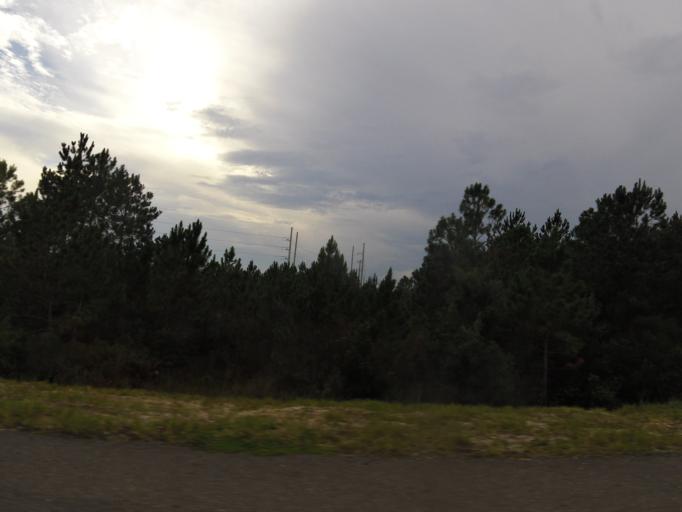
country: US
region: Florida
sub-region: Duval County
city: Baldwin
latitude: 30.3046
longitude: -81.8832
